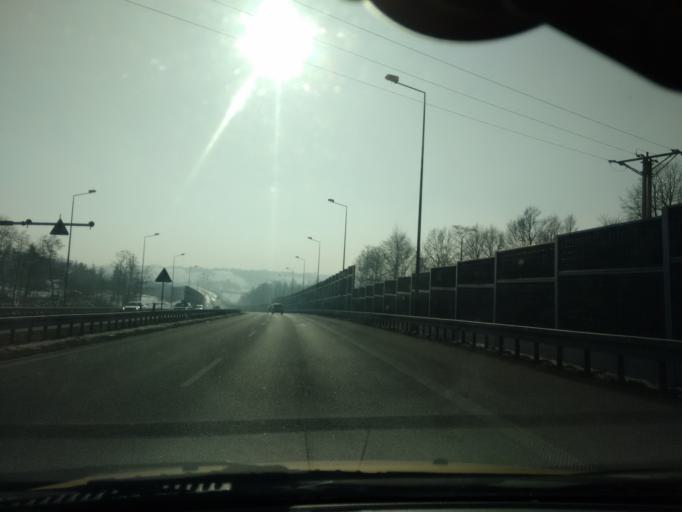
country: PL
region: Silesian Voivodeship
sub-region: Bielsko-Biala
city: Bielsko-Biala
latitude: 49.8393
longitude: 19.0879
